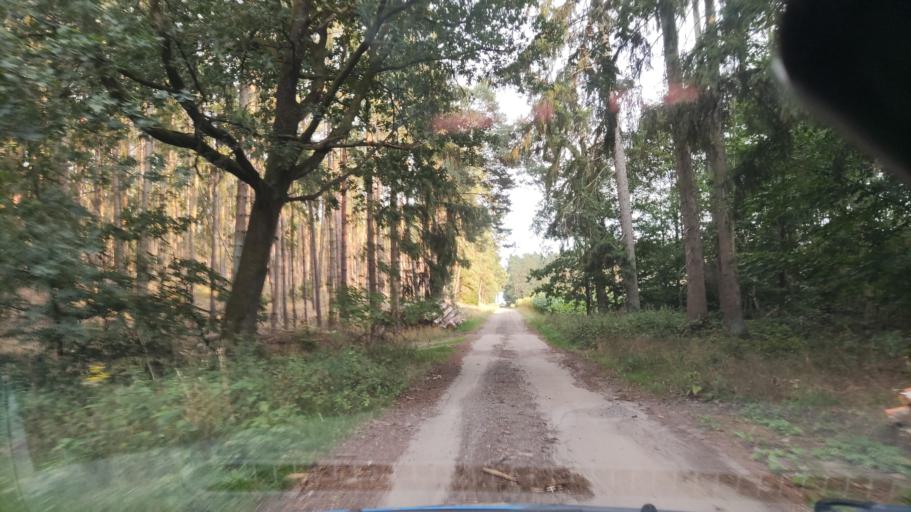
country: DE
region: Lower Saxony
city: Dahlem
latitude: 53.2157
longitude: 10.7330
